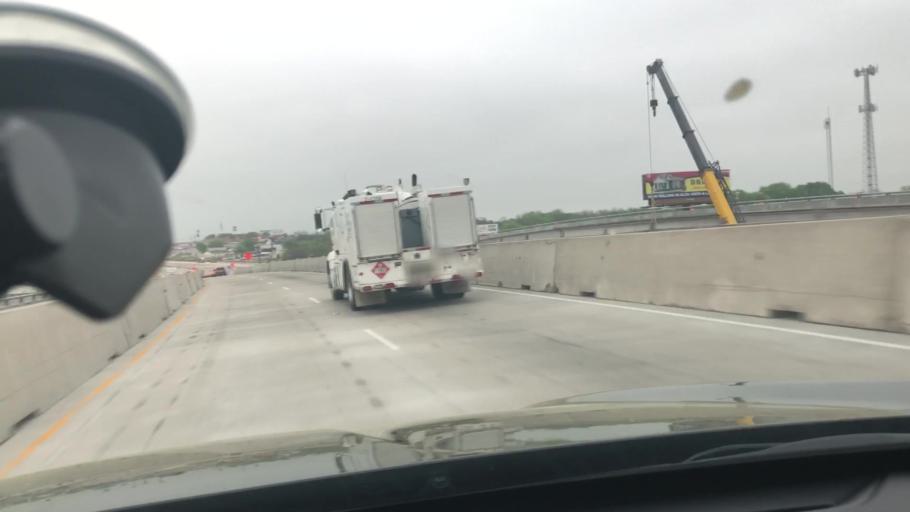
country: US
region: Texas
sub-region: Bell County
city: Temple
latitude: 31.0973
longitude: -97.3656
